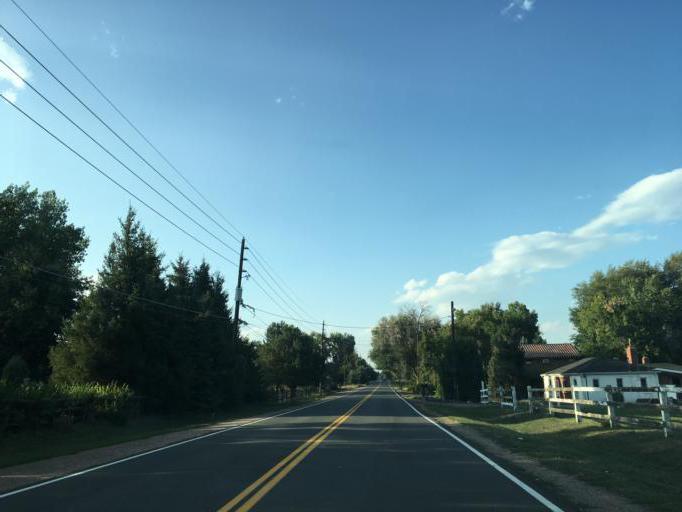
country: US
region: Colorado
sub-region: Jefferson County
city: Applewood
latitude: 39.7874
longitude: -105.1653
